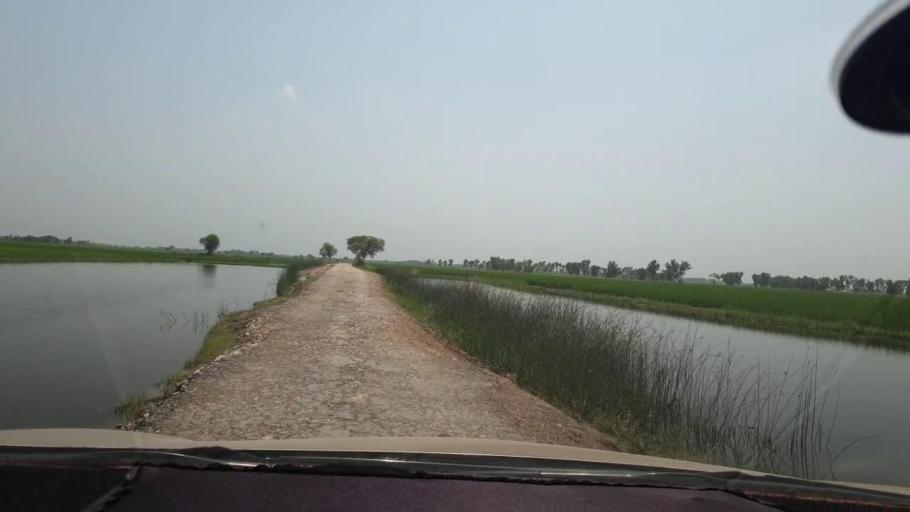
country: PK
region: Sindh
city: Kambar
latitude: 27.6553
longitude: 67.9305
